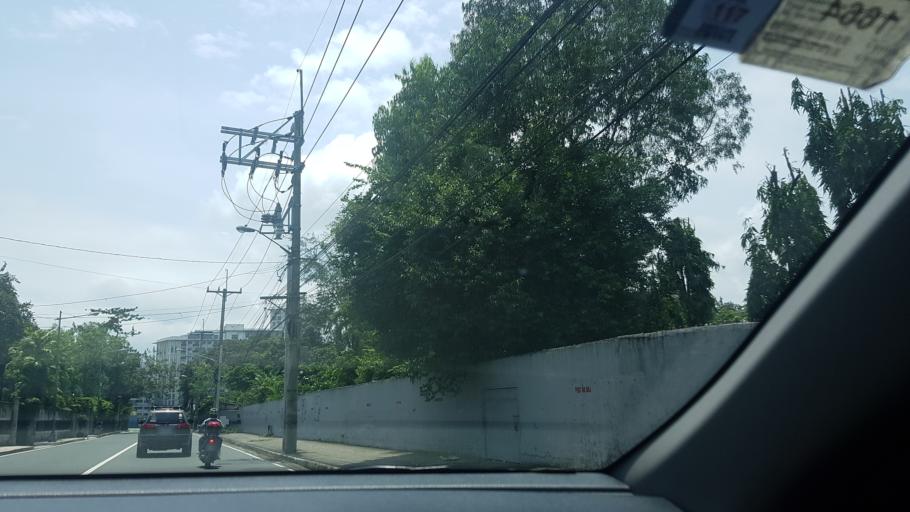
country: PH
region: Metro Manila
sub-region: San Juan
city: San Juan
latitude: 14.6050
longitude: 121.0345
